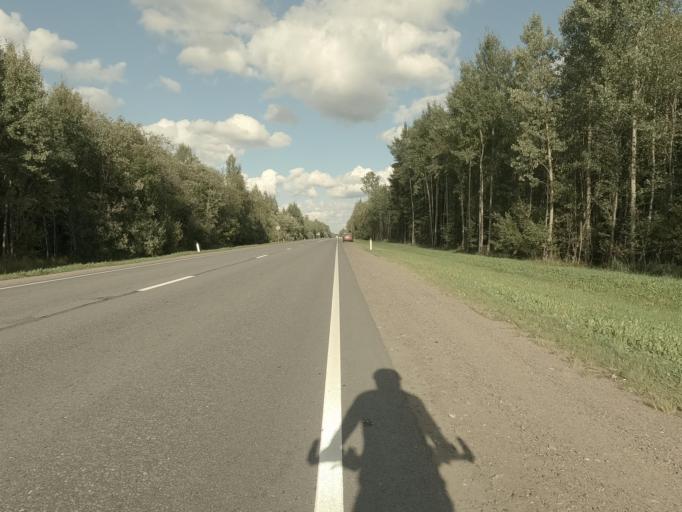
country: RU
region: Leningrad
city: Nikol'skoye
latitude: 59.6696
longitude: 30.8970
